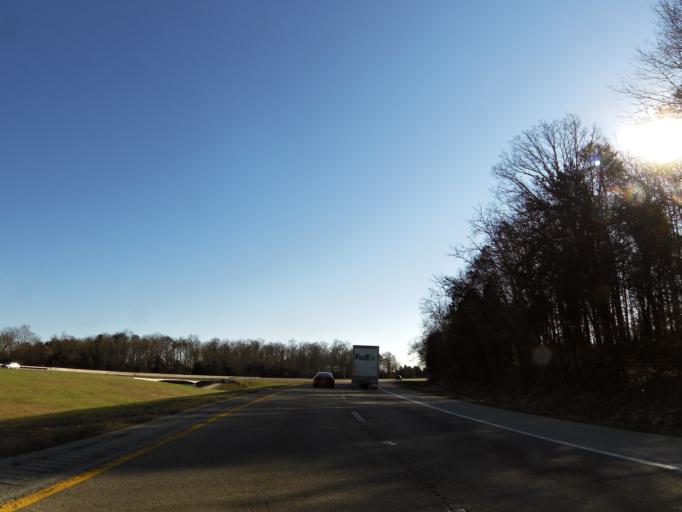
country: US
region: Tennessee
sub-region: Jefferson County
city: Dandridge
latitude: 36.0672
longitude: -83.3858
